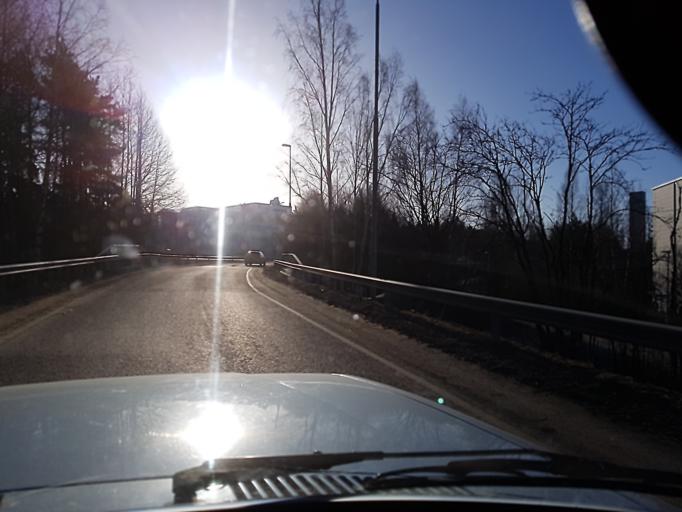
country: FI
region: Uusimaa
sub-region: Helsinki
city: Teekkarikylae
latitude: 60.2621
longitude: 24.8741
